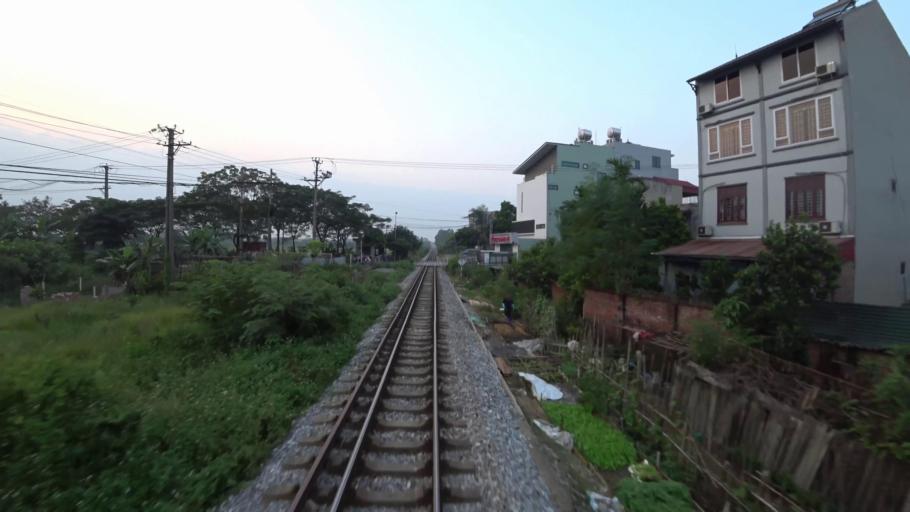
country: VN
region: Ha Noi
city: Dong Anh
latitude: 21.1486
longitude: 105.8577
